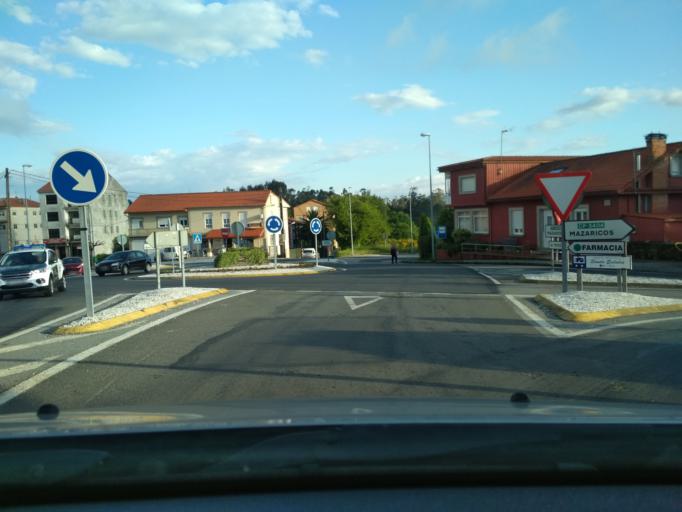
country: ES
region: Galicia
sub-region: Provincia da Coruna
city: Mazaricos
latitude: 42.9079
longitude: -8.9546
